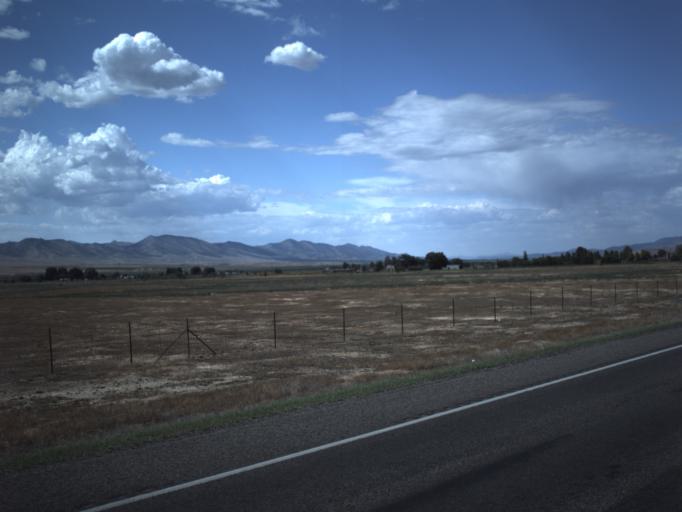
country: US
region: Utah
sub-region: Sevier County
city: Salina
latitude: 39.0369
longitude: -111.8278
